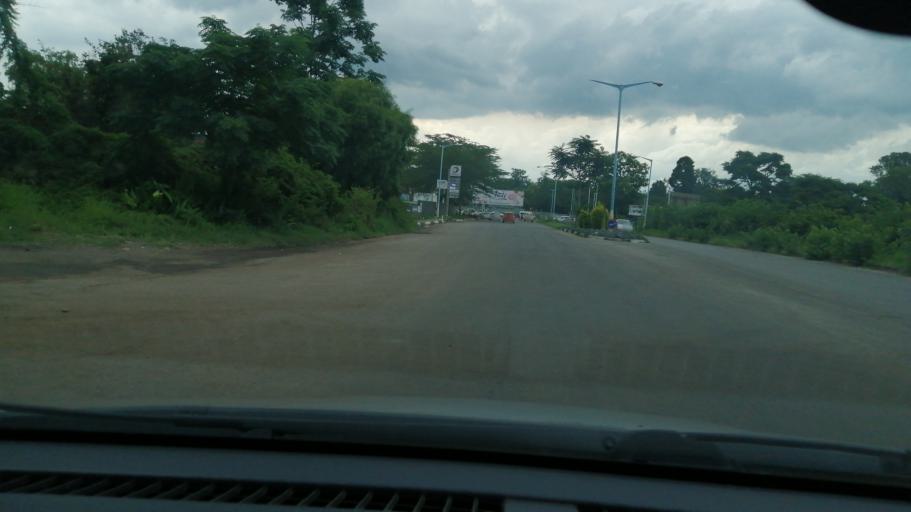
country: ZW
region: Harare
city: Harare
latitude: -17.7912
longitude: 31.0452
